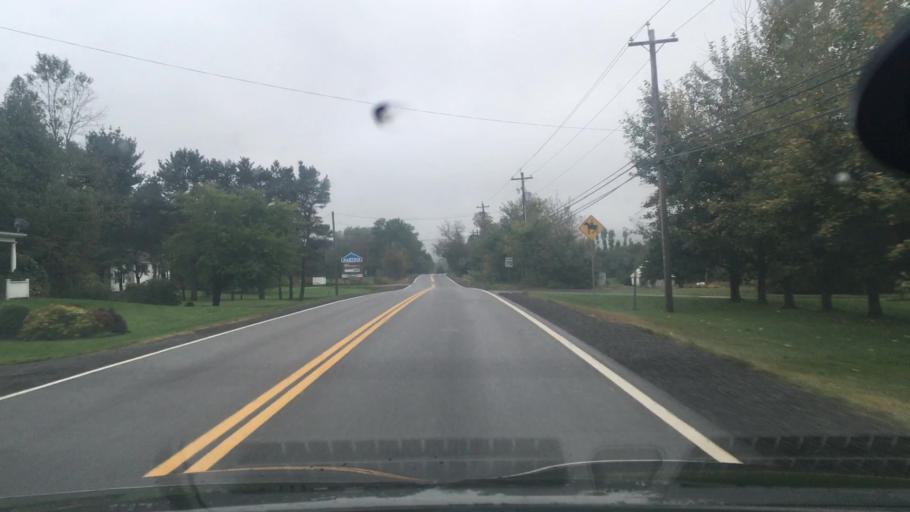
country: CA
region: Nova Scotia
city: Windsor
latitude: 44.9404
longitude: -64.1886
